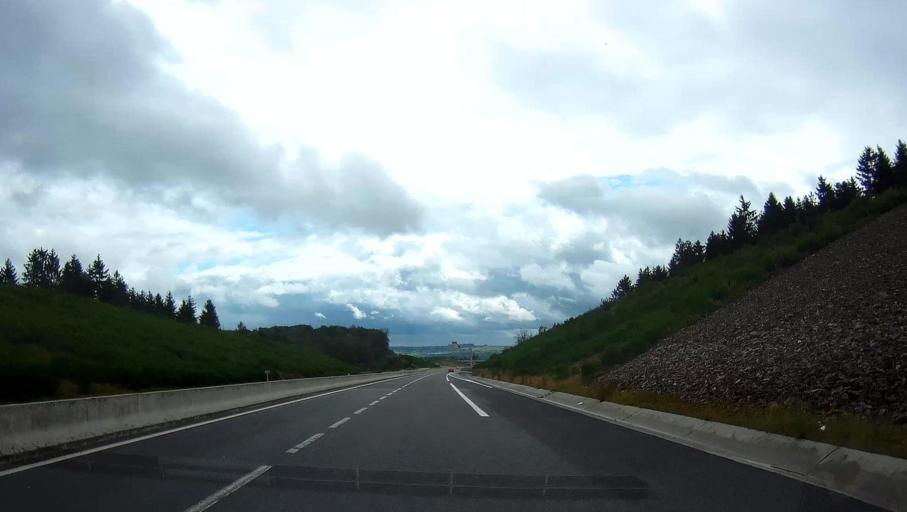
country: FR
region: Champagne-Ardenne
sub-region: Departement des Ardennes
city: Rimogne
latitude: 49.8517
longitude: 4.5130
